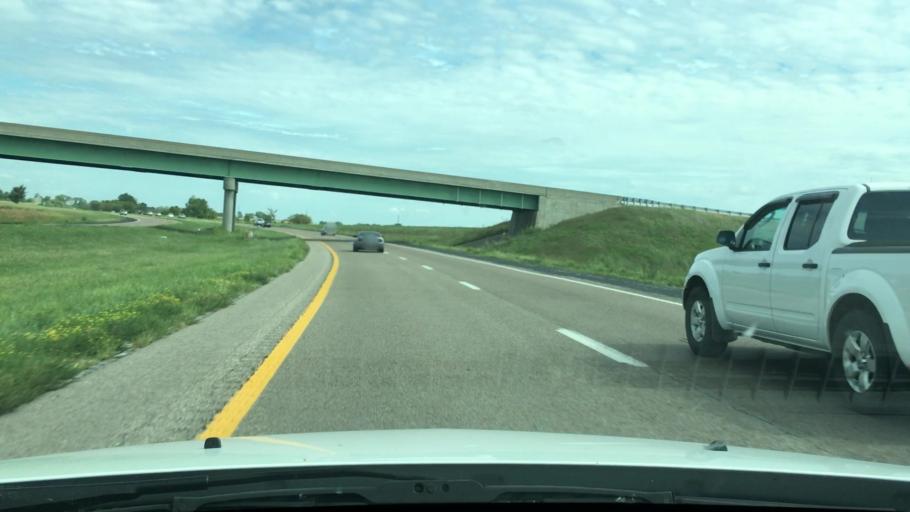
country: US
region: Missouri
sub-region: Audrain County
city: Mexico
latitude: 39.0173
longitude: -91.8866
